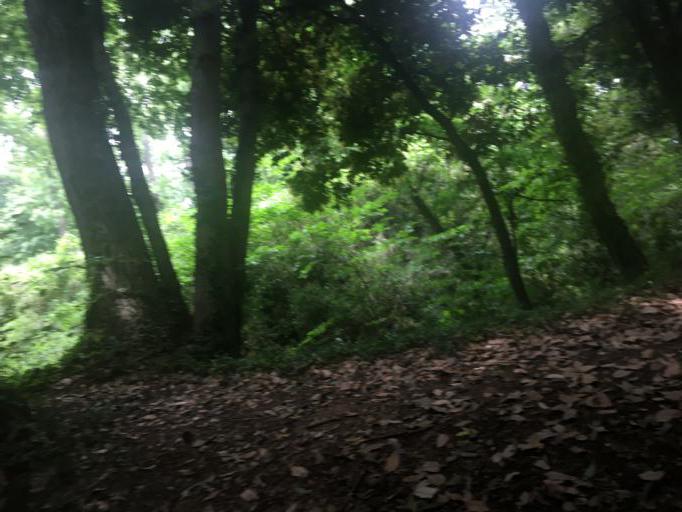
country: JP
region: Saitama
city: Fukiage-fujimi
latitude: 36.0371
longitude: 139.4222
